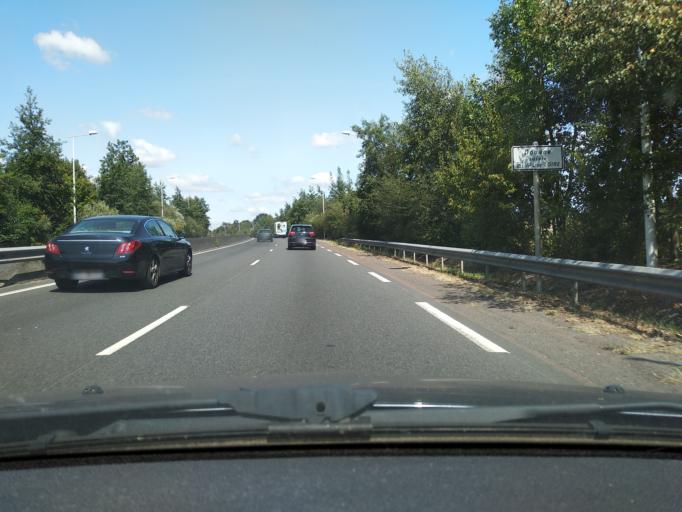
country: FR
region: Centre
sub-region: Departement d'Indre-et-Loire
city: Rochecorbon
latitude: 47.4113
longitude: 0.7208
